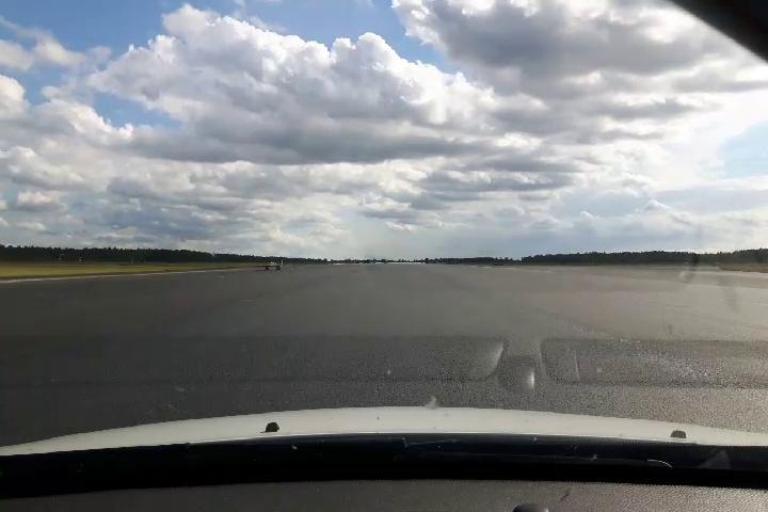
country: SE
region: Stockholm
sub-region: Sigtuna Kommun
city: Rosersberg
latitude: 59.6298
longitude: 17.9519
